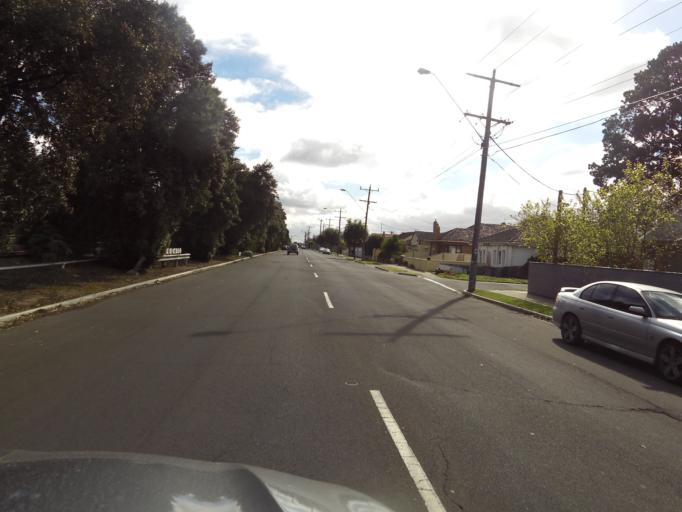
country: AU
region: Victoria
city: Spotswood
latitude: -37.8335
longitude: 144.8854
